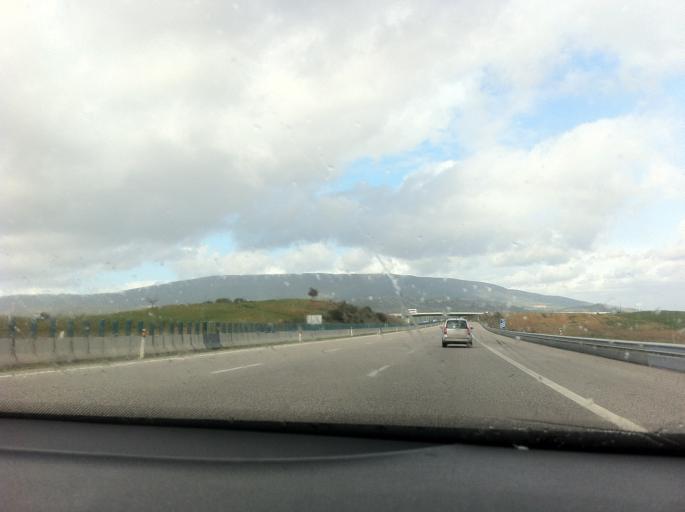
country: PT
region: Santarem
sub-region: Alcanena
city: Alcanena
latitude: 39.4648
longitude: -8.6293
